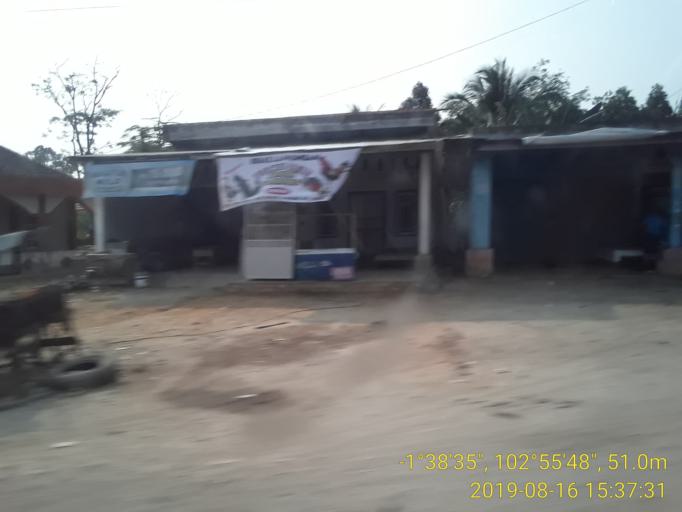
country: ID
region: Jambi
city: Mersam
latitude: -1.6432
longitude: 102.9302
